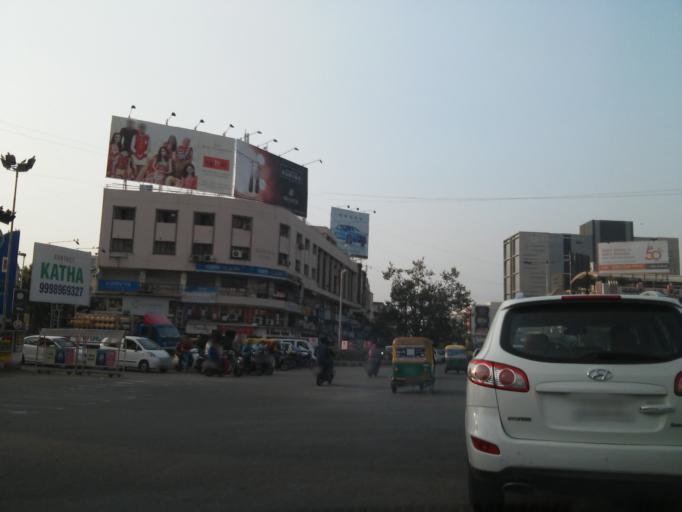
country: IN
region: Gujarat
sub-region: Ahmadabad
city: Sarkhej
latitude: 23.0319
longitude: 72.5253
